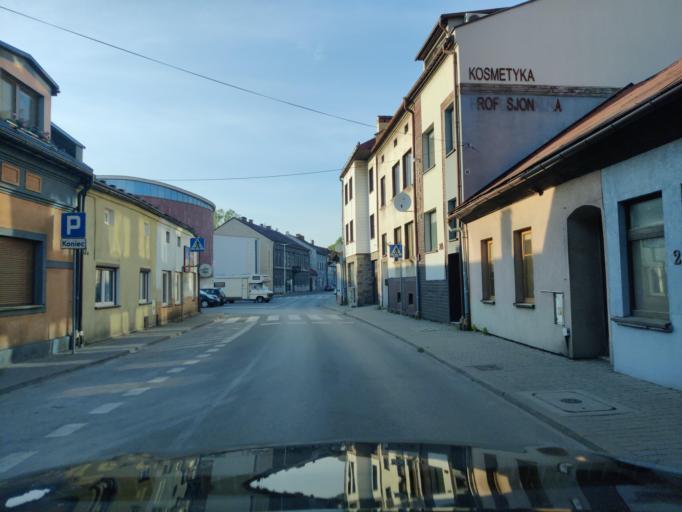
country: PL
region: Silesian Voivodeship
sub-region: Powiat zywiecki
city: Zywiec
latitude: 49.6906
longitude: 19.2032
